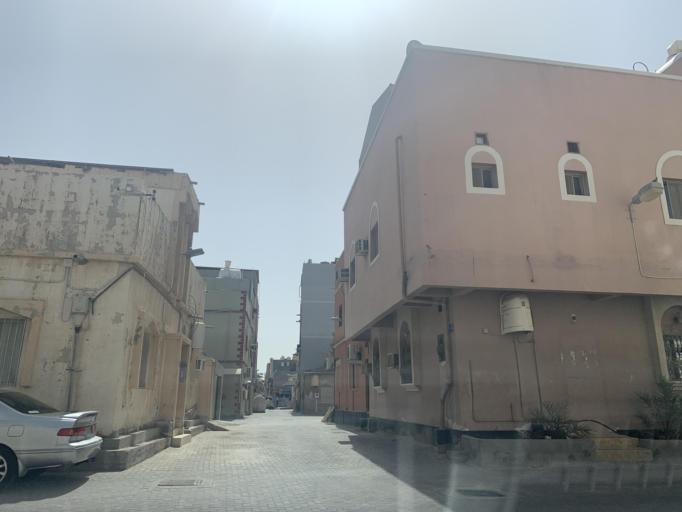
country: BH
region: Northern
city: Sitrah
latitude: 26.1602
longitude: 50.6087
